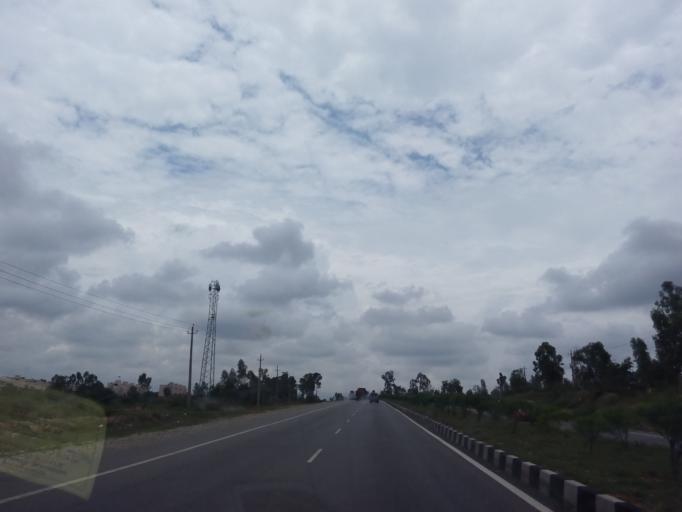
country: IN
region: Karnataka
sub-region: Hassan
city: Channarayapatna
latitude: 12.9742
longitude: 76.2753
